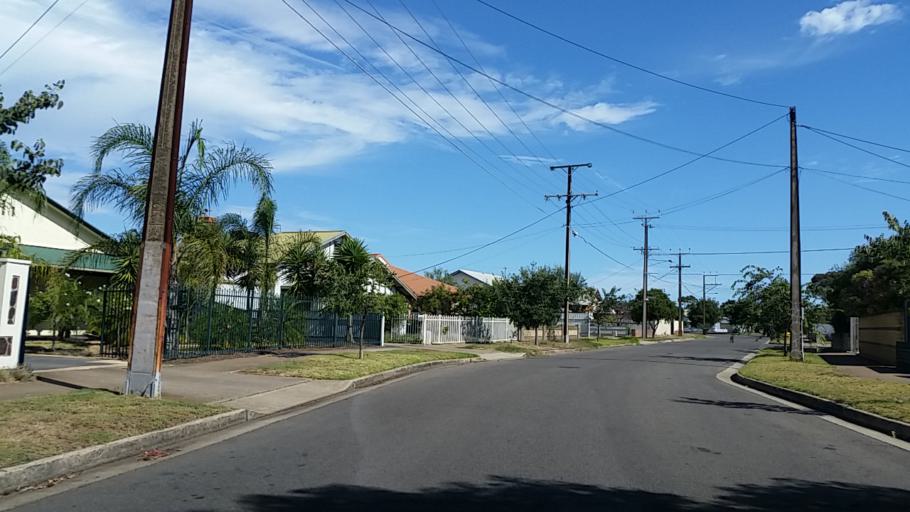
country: AU
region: South Australia
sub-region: Port Adelaide Enfield
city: Alberton
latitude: -34.8526
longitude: 138.5317
